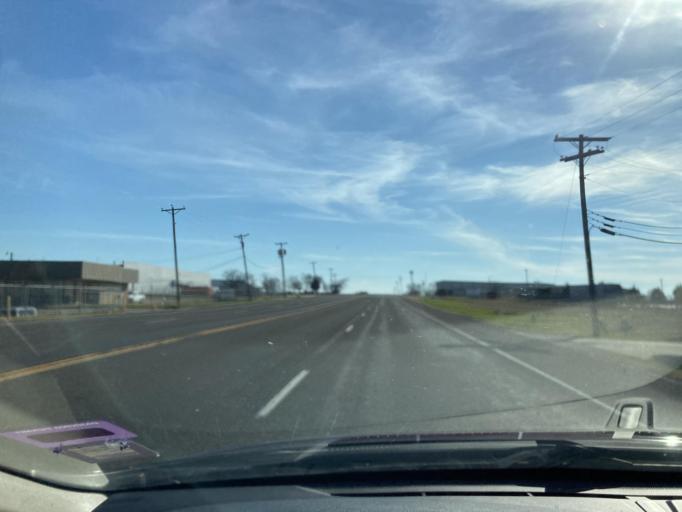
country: US
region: Texas
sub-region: Navarro County
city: Corsicana
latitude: 32.0725
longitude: -96.4531
